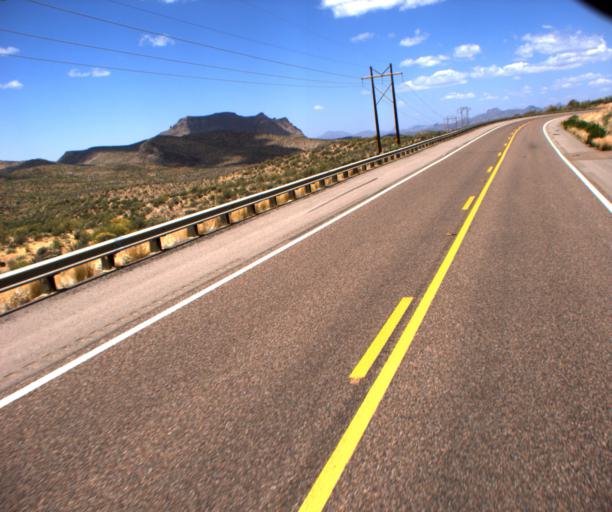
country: US
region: Arizona
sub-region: Pinal County
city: Superior
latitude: 33.2352
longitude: -111.0939
